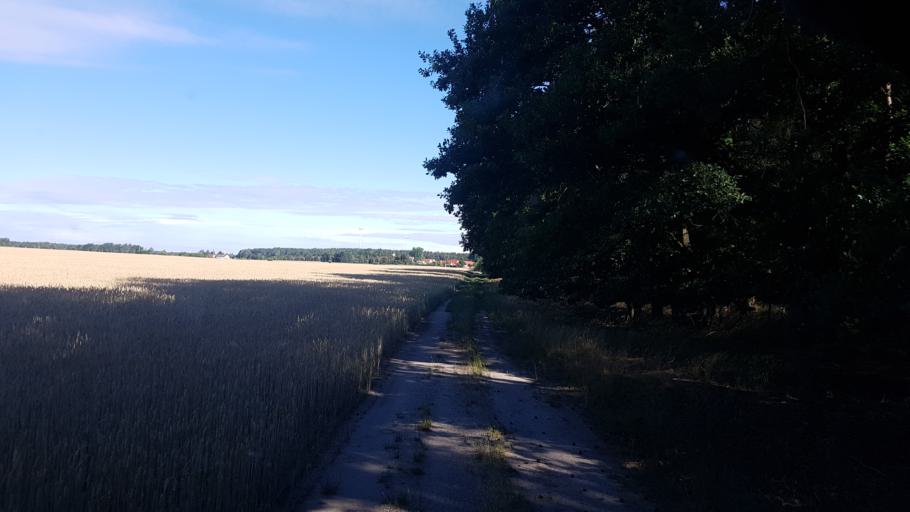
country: DE
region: Brandenburg
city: Sallgast
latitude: 51.6098
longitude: 13.8163
